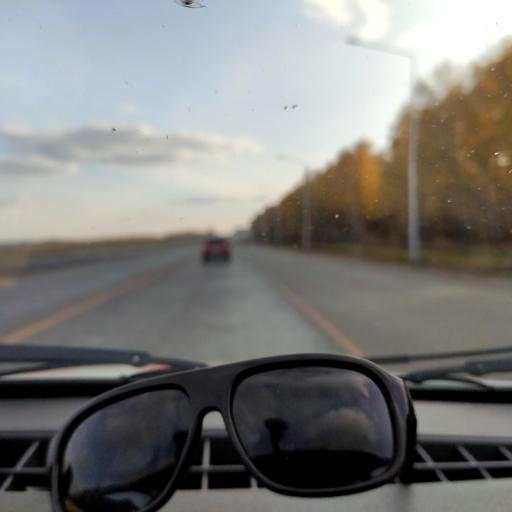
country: RU
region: Bashkortostan
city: Tolbazy
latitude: 54.1351
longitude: 55.9024
